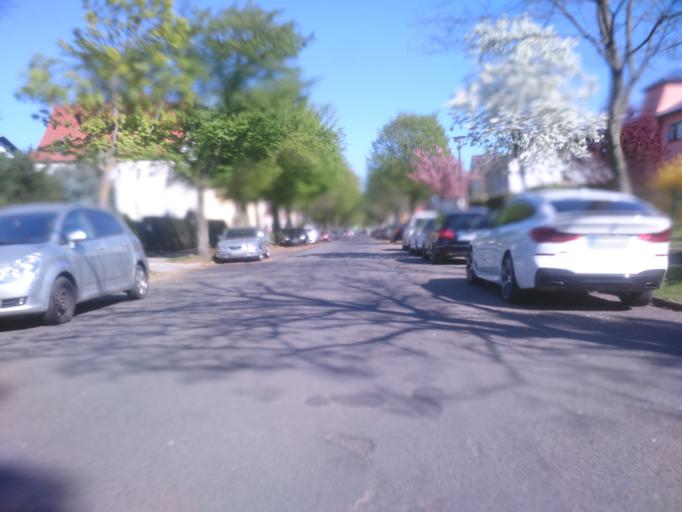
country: DE
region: Berlin
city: Weissensee
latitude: 52.5630
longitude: 13.4789
